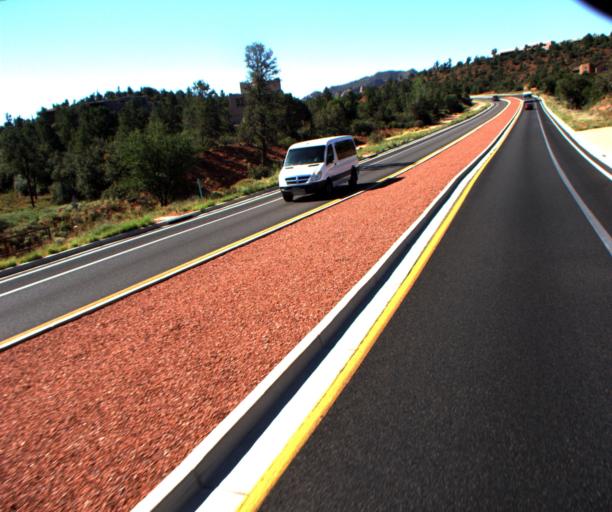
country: US
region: Arizona
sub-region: Coconino County
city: Sedona
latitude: 34.8389
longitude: -111.7766
